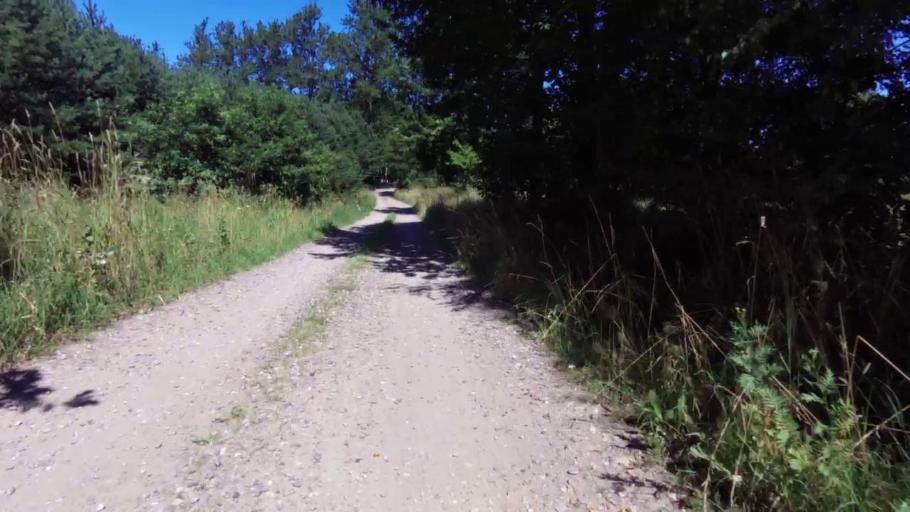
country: PL
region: West Pomeranian Voivodeship
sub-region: Powiat drawski
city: Wierzchowo
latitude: 53.5242
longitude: 16.1416
